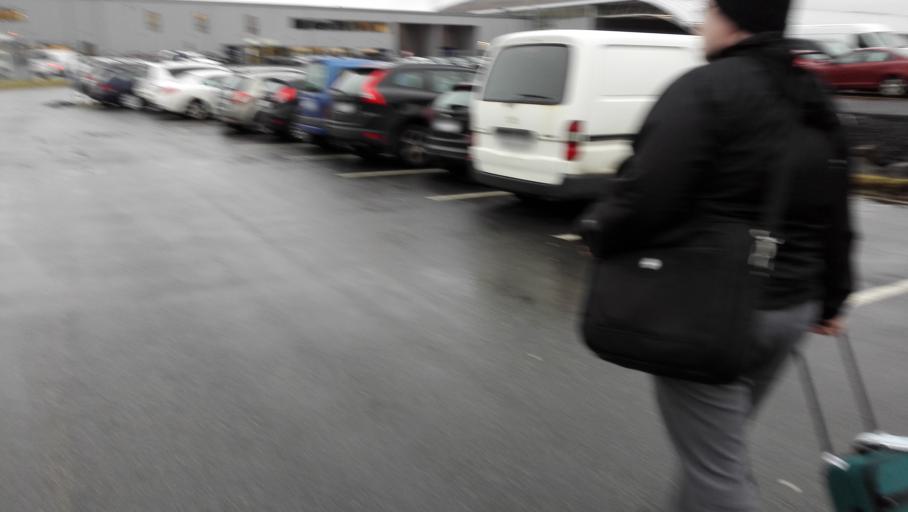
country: FO
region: Vagar
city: Midvagur
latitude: 62.0677
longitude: -7.2763
